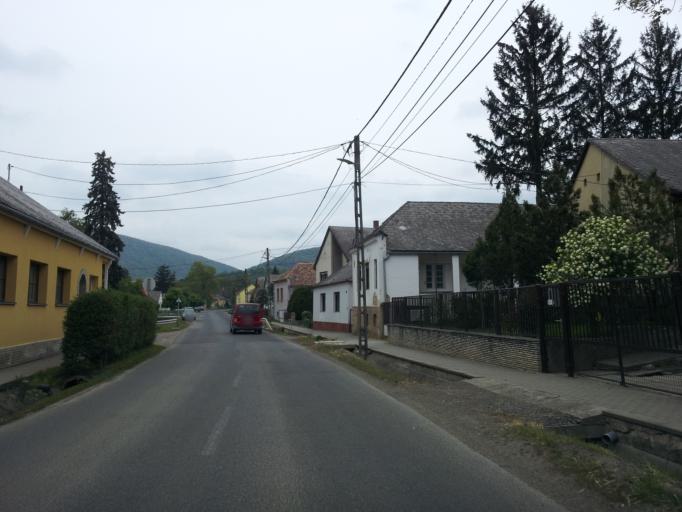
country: HU
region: Baranya
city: Hosszuheteny
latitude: 46.1564
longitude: 18.3550
